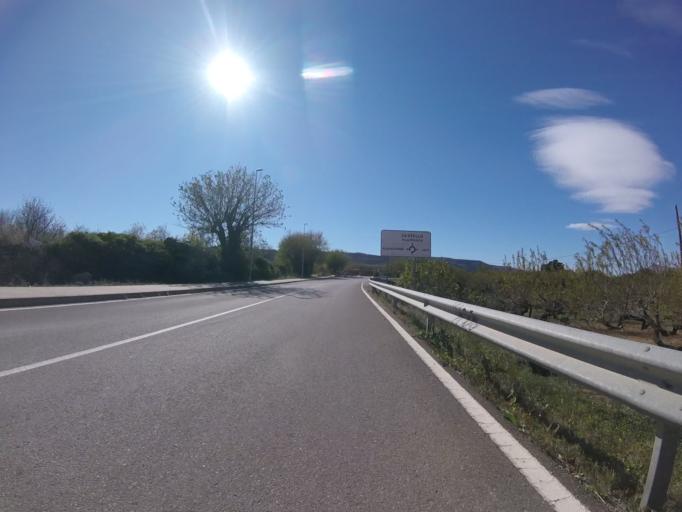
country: ES
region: Valencia
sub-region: Provincia de Castello
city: Albocasser
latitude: 40.3631
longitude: 0.0218
